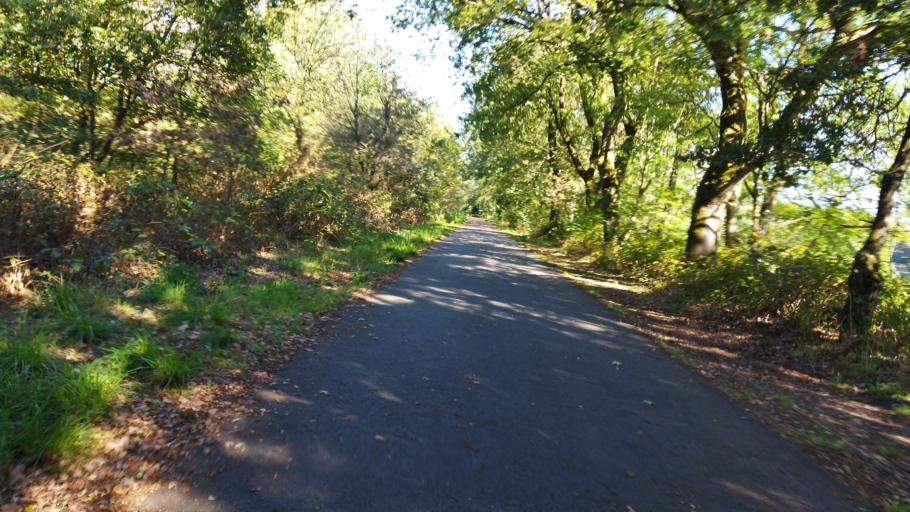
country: DE
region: Lower Saxony
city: Ohne
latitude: 52.2701
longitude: 7.3147
